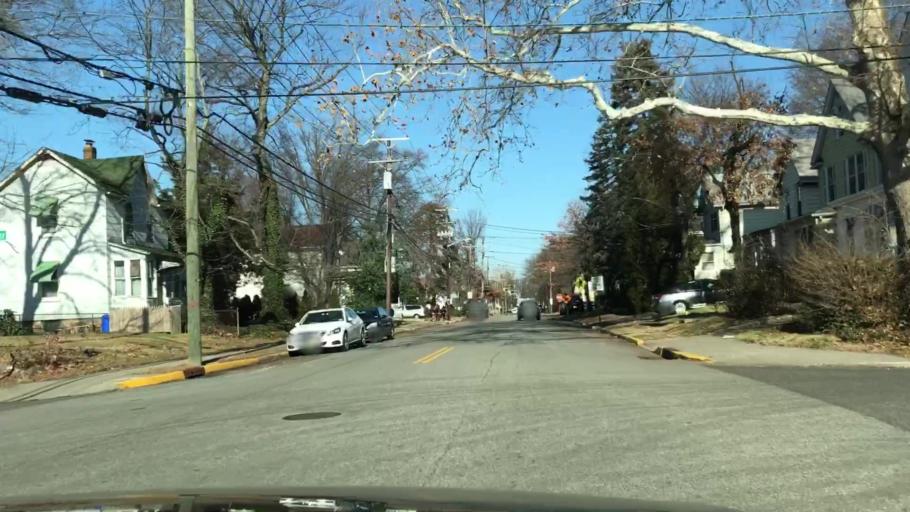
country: US
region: New Jersey
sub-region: Bergen County
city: Tenafly
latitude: 40.9276
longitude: -73.9654
